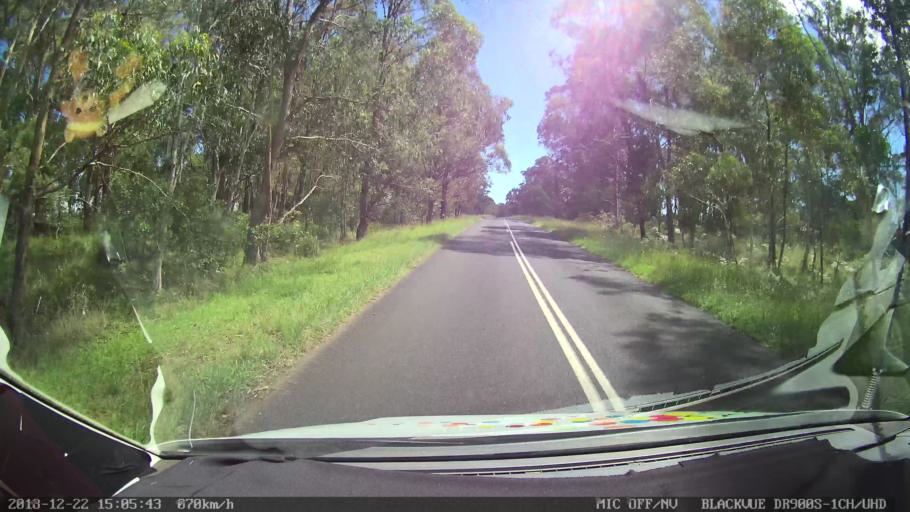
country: AU
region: New South Wales
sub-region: Bellingen
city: Dorrigo
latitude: -30.2868
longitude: 152.4334
